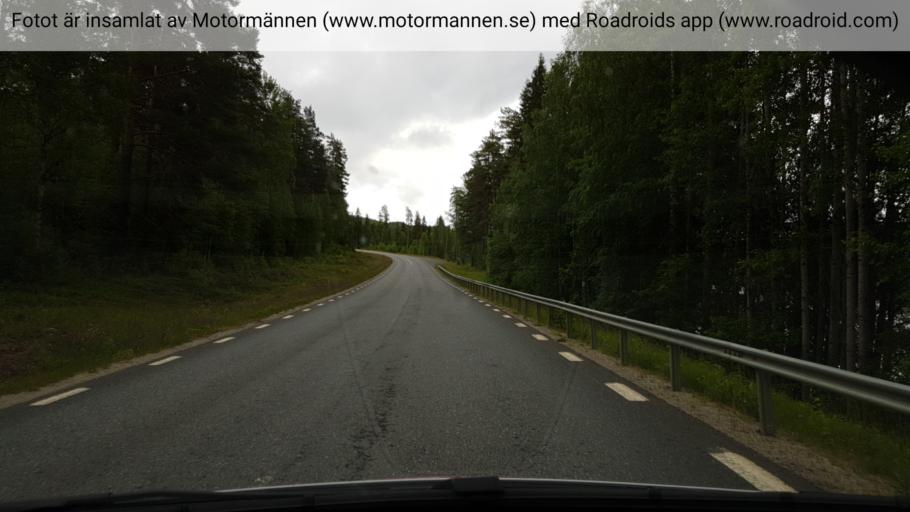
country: SE
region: Vaesterbotten
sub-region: Lycksele Kommun
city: Lycksele
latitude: 64.4305
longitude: 18.9773
